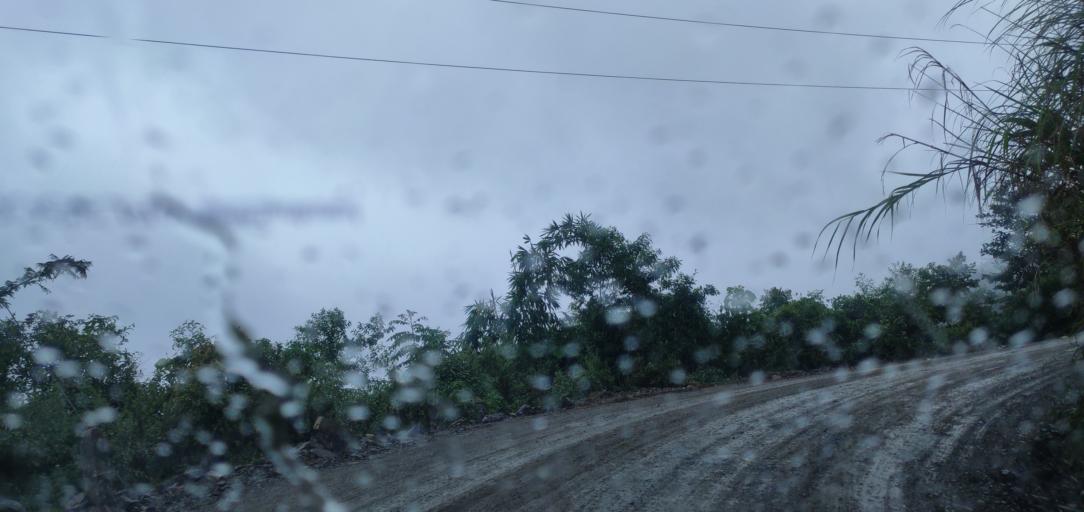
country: LA
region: Phongsali
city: Phongsali
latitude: 21.4300
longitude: 102.1616
